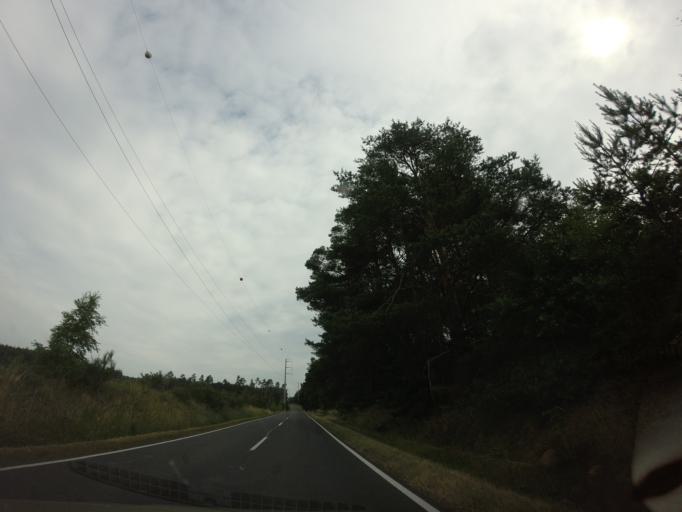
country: PL
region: West Pomeranian Voivodeship
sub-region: Powiat walecki
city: Miroslawiec
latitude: 53.3642
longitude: 16.1211
